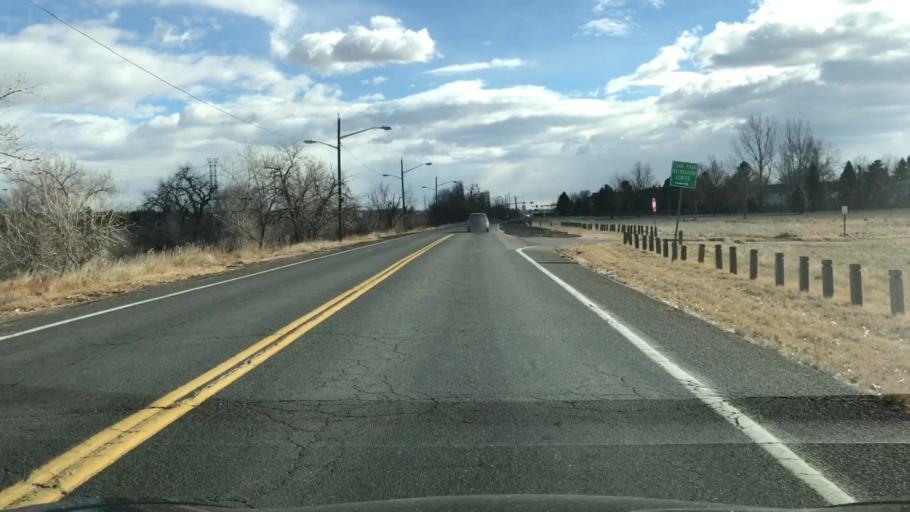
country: US
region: Colorado
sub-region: Arapahoe County
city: Glendale
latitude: 39.6874
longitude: -104.9076
